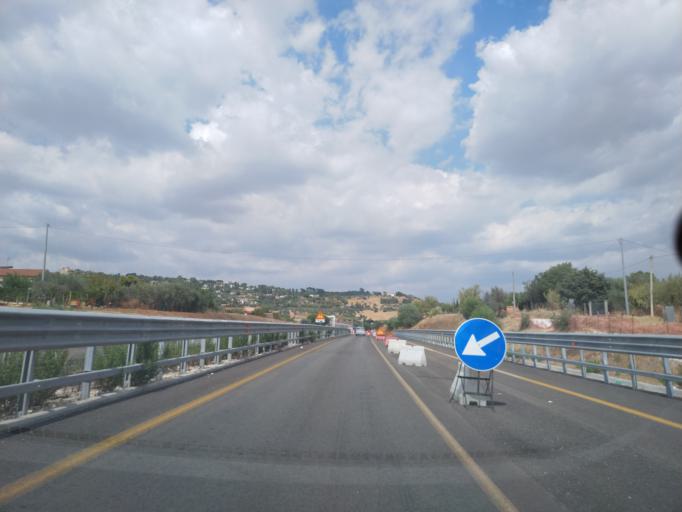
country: IT
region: Sicily
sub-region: Provincia di Caltanissetta
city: San Cataldo
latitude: 37.4700
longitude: 14.0097
